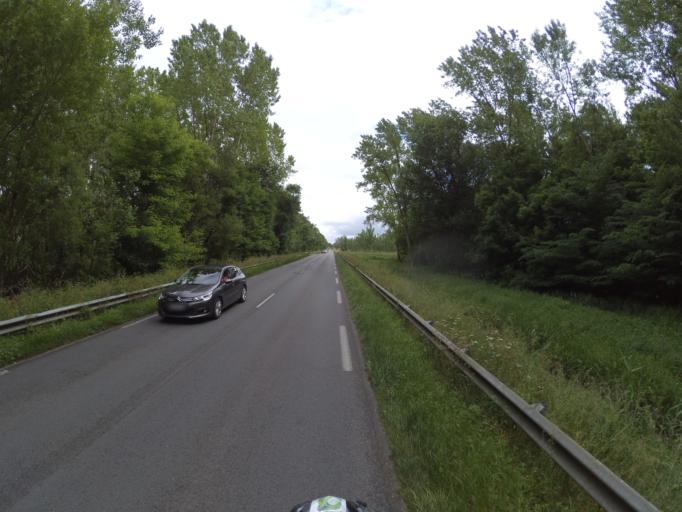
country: FR
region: Aquitaine
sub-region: Departement de la Gironde
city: Soussans
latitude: 45.0649
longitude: -0.7200
